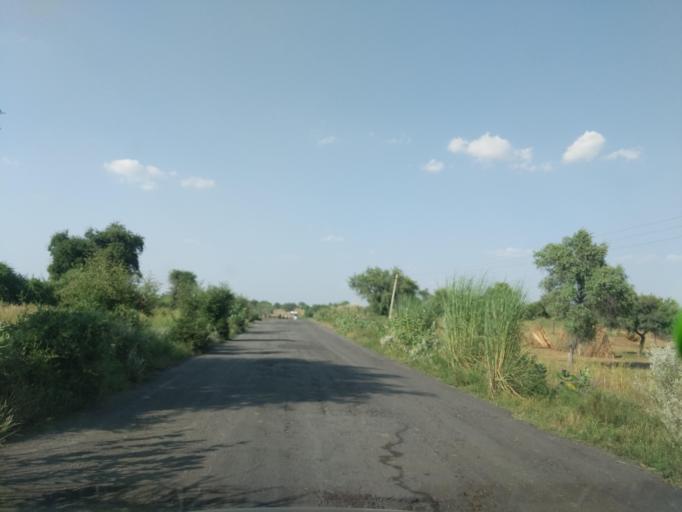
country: IN
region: Rajasthan
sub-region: Churu
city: Rajgarh
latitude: 28.4839
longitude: 75.3693
